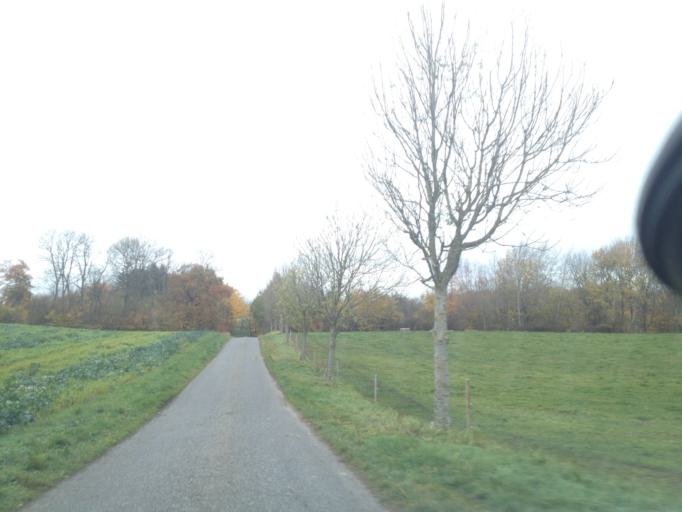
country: DK
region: South Denmark
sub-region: Assens Kommune
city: Vissenbjerg
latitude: 55.4290
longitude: 10.1677
